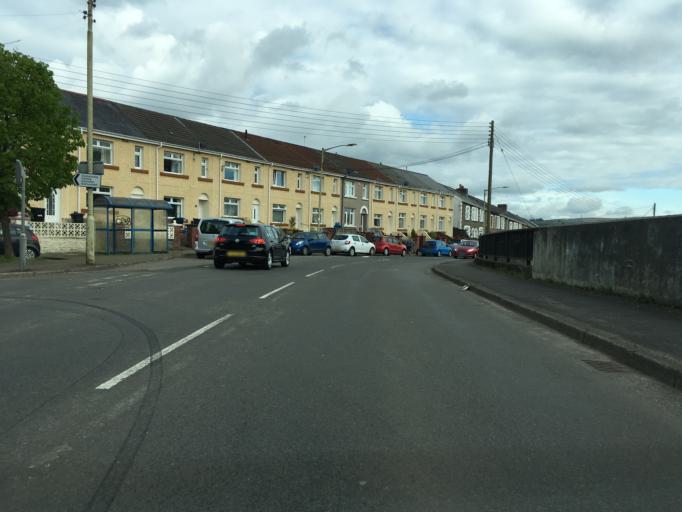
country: GB
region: Wales
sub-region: Caerphilly County Borough
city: Nelson
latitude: 51.6621
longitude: -3.2920
